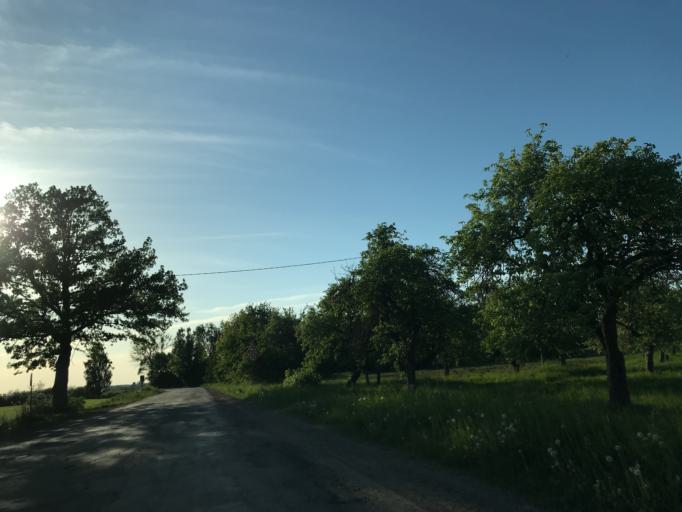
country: LV
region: Ozolnieku
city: Ozolnieki
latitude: 56.5674
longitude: 23.8591
